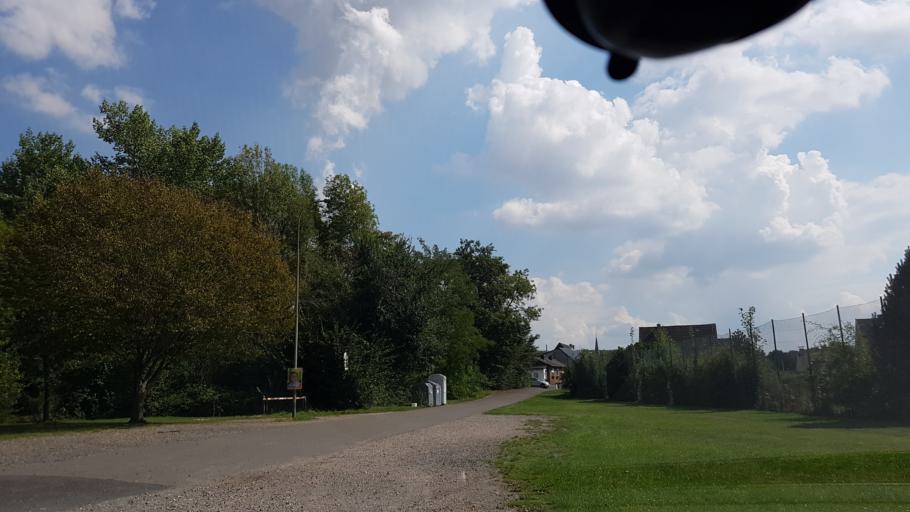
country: DE
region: North Rhine-Westphalia
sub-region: Regierungsbezirk Dusseldorf
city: Grevenbroich
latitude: 51.0422
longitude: 6.5893
